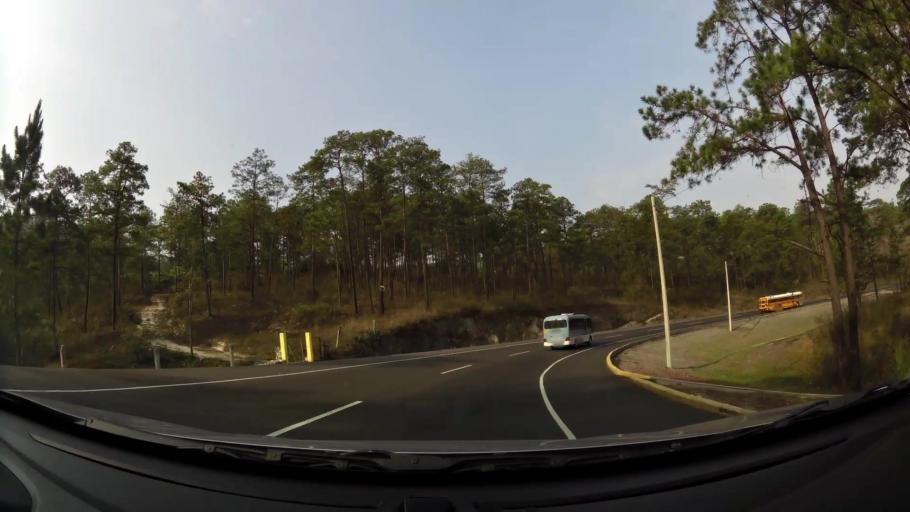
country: HN
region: Francisco Morazan
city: Zambrano
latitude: 14.2868
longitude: -87.4727
